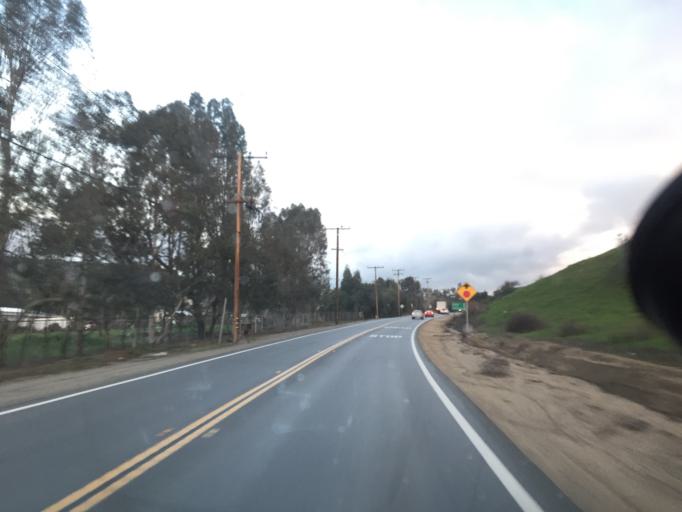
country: US
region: California
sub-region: San Bernardino County
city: Redlands
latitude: 33.9935
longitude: -117.1560
